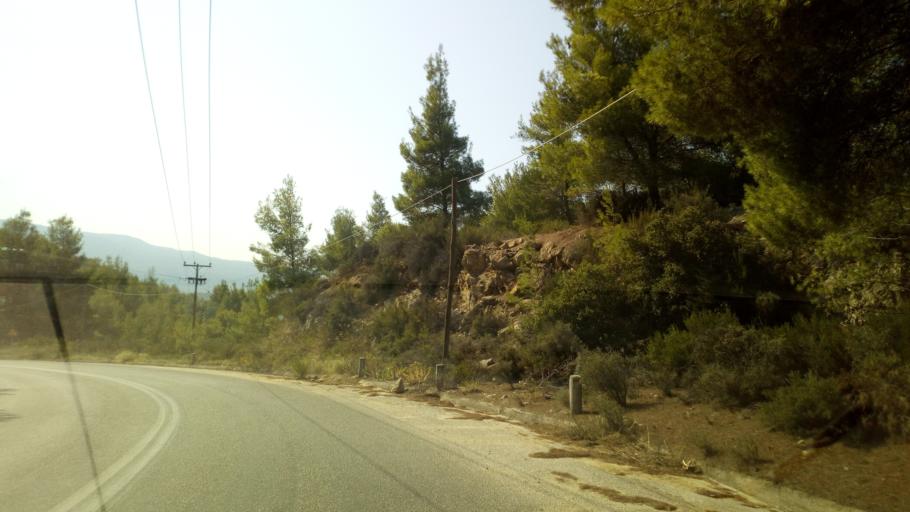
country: GR
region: Central Macedonia
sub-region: Nomos Chalkidikis
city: Sarti
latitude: 40.1137
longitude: 23.9826
